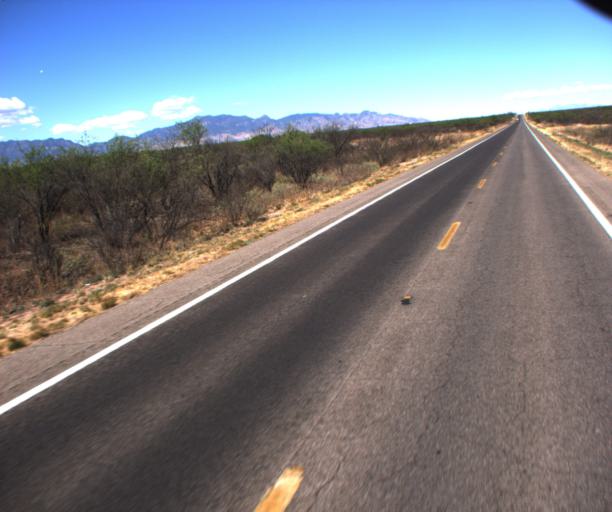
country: US
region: Arizona
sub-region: Cochise County
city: Sierra Vista Southeast
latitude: 31.5485
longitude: -110.1712
